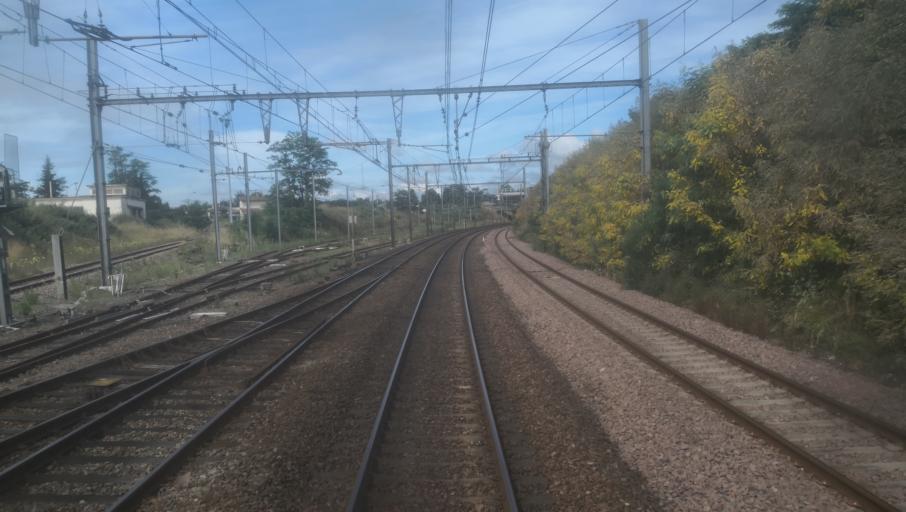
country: FR
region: Aquitaine
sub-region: Departement de la Gironde
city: Toulenne
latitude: 44.5538
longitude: -0.2606
